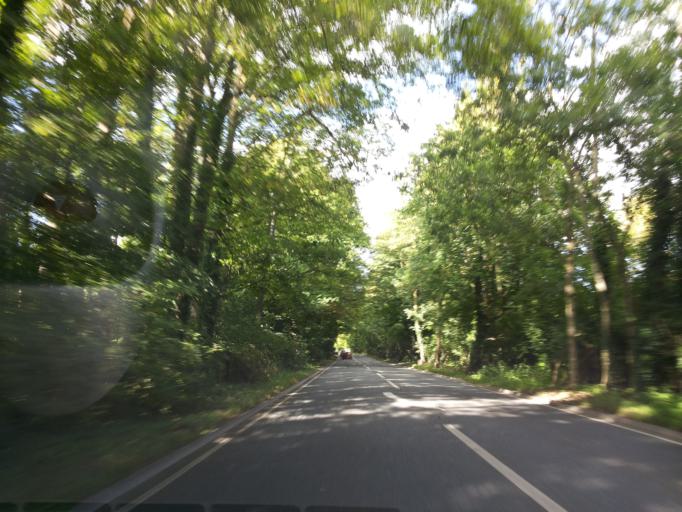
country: GB
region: England
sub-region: Bath and North East Somerset
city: Freshford
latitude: 51.3274
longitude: -2.3120
